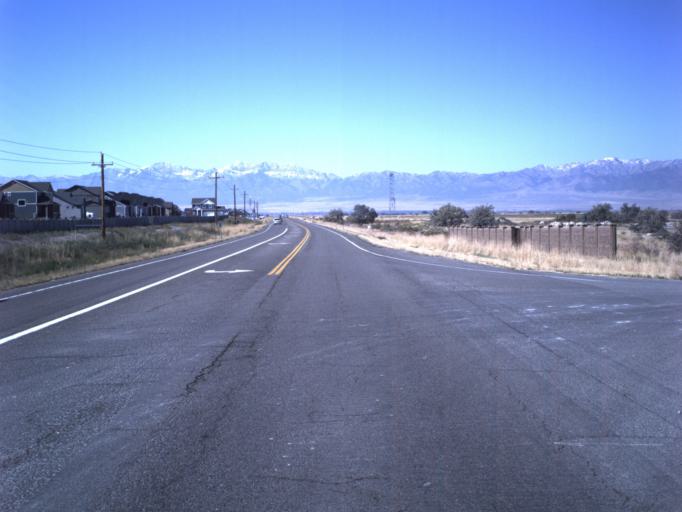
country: US
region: Utah
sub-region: Tooele County
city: Stansbury park
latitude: 40.6434
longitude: -112.3119
